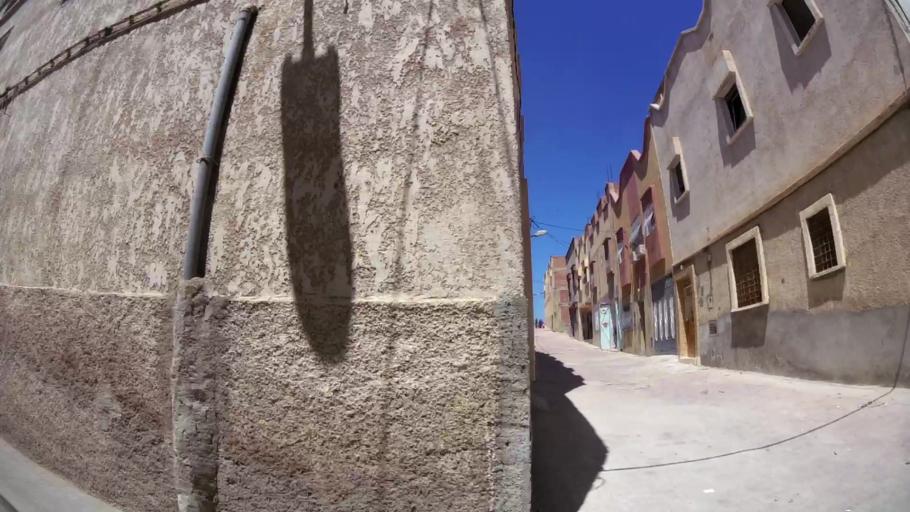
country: MA
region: Oriental
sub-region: Oujda-Angad
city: Oujda
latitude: 34.6824
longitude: -1.9548
